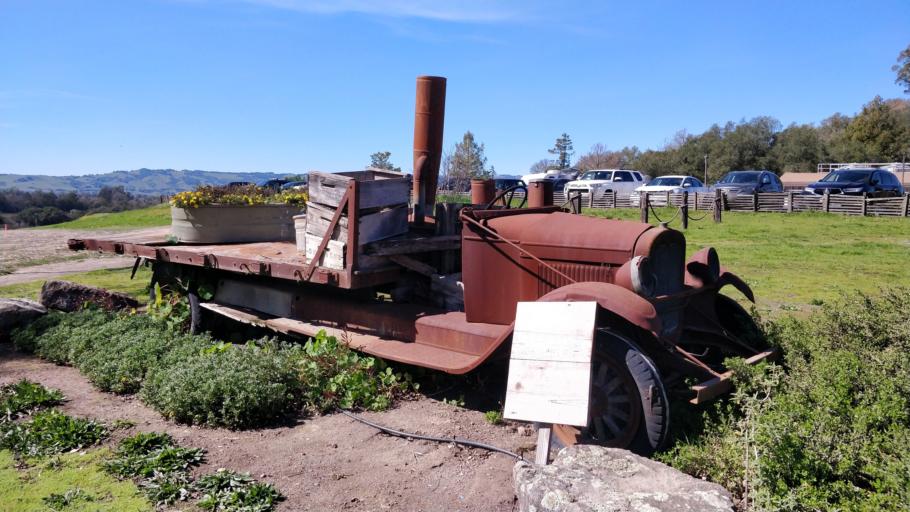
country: US
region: California
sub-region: Sonoma County
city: Sonoma
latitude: 38.2802
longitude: -122.4169
